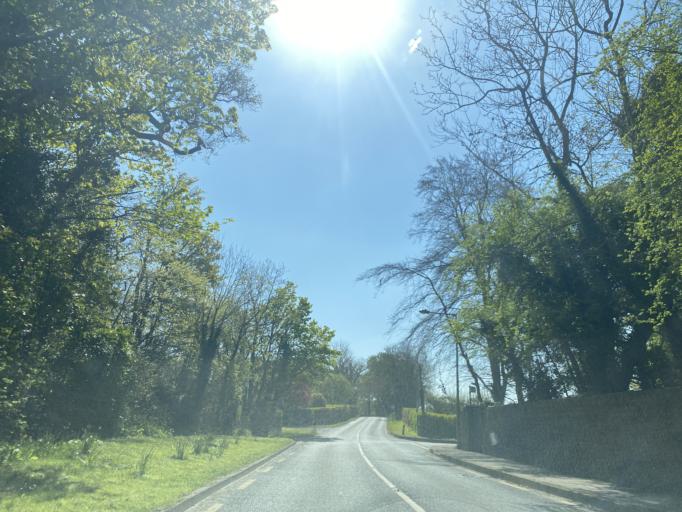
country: IE
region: Leinster
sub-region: Kildare
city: Kill
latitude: 53.3042
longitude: -6.6140
